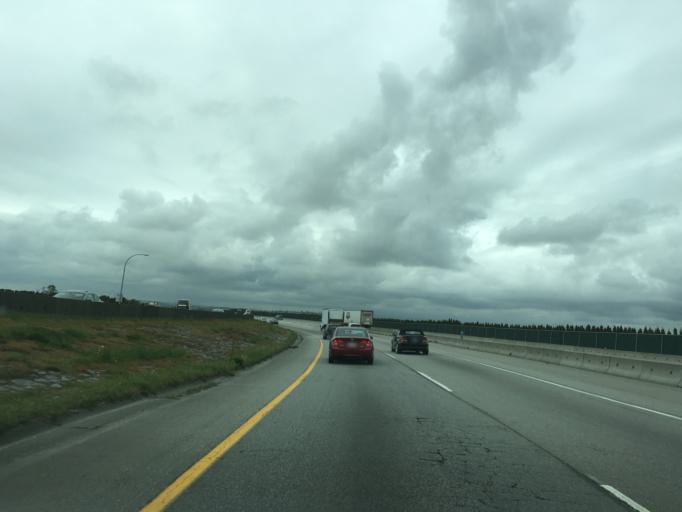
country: CA
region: British Columbia
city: New Westminster
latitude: 49.1752
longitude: -123.0138
